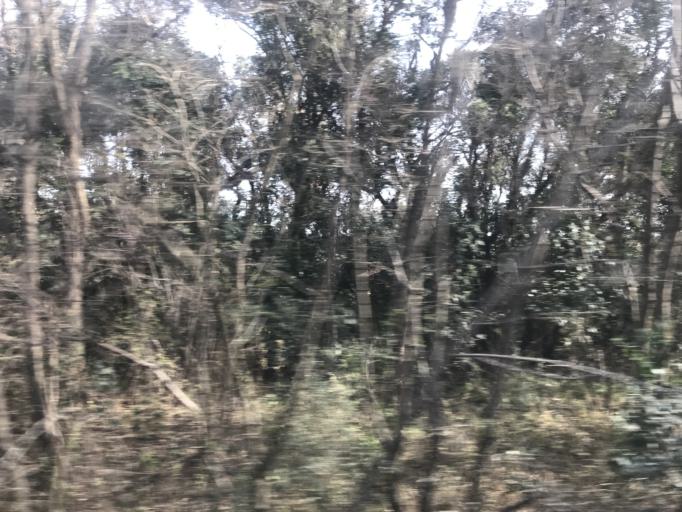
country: AR
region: Cordoba
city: Laguna Larga
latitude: -31.7640
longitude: -63.8142
